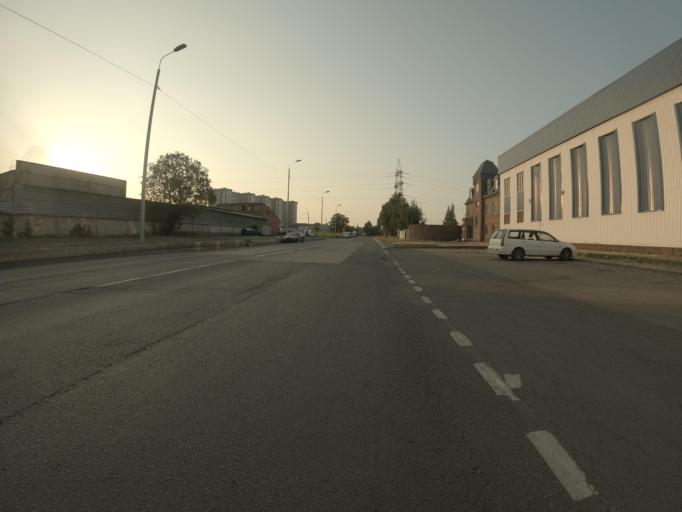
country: RU
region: St.-Petersburg
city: Krasnogvargeisky
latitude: 59.9733
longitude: 30.4408
